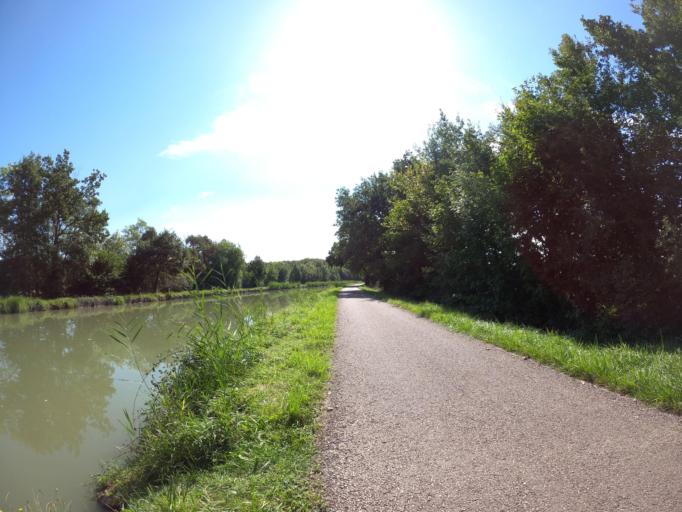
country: FR
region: Midi-Pyrenees
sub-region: Departement du Tarn-et-Garonne
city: Montech
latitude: 43.9471
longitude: 1.2527
